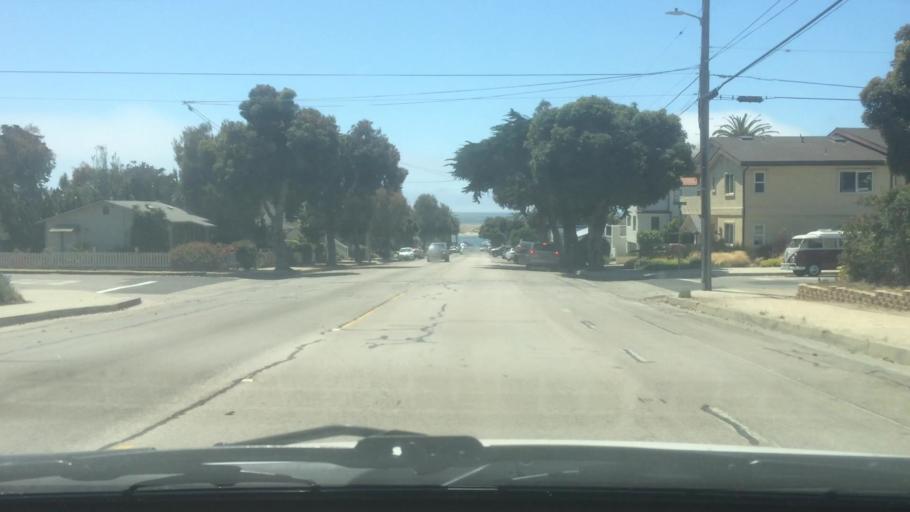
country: US
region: California
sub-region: San Luis Obispo County
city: Morro Bay
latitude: 35.3651
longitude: -120.8474
